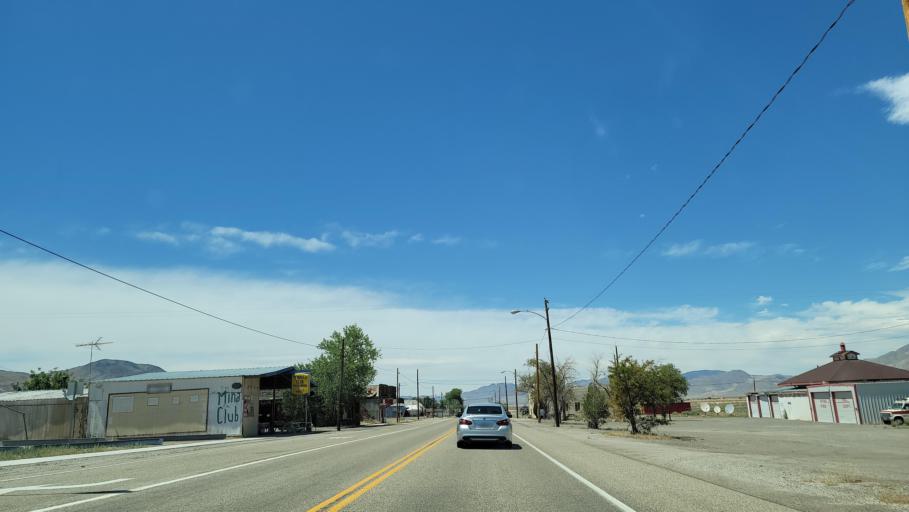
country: US
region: Nevada
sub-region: Mineral County
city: Hawthorne
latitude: 38.3900
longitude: -118.1083
